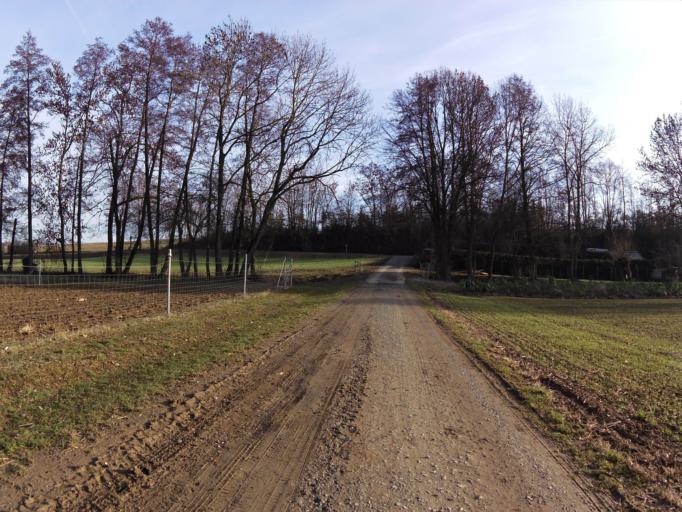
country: DE
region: Bavaria
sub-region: Regierungsbezirk Unterfranken
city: Estenfeld
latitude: 49.8366
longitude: 10.0177
